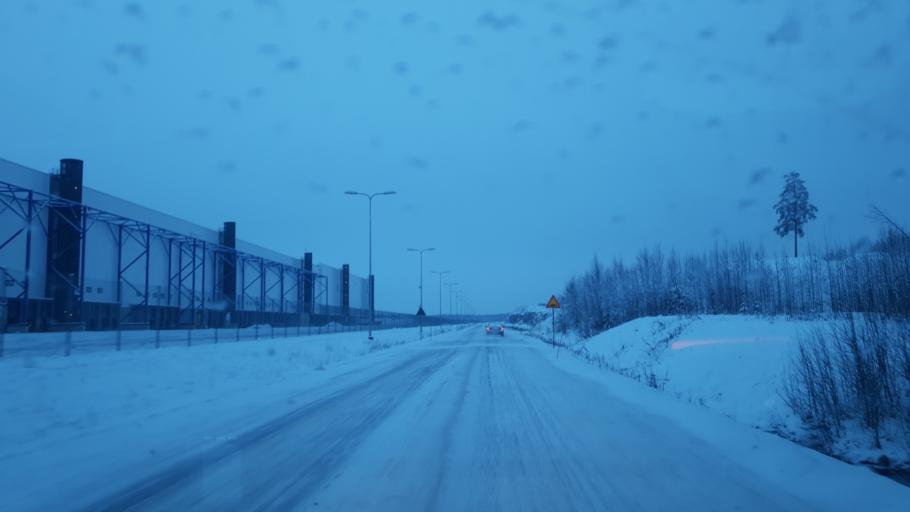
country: FI
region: Uusimaa
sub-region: Helsinki
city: Kerava
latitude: 60.3738
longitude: 25.1554
